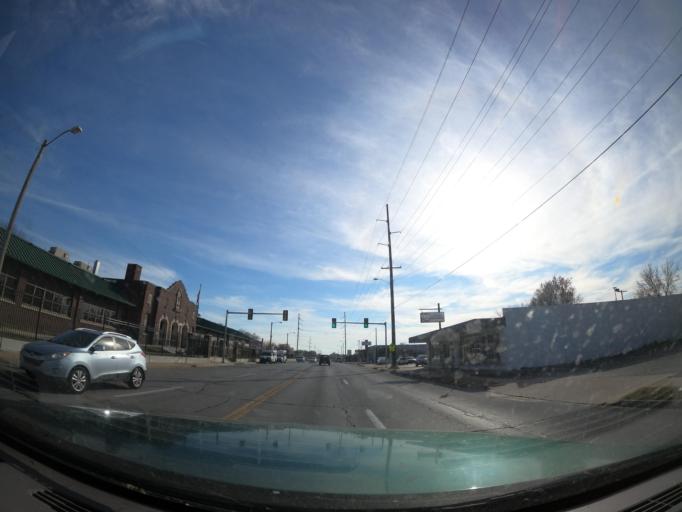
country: US
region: Oklahoma
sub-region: Tulsa County
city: Tulsa
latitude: 36.1363
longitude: -95.9404
